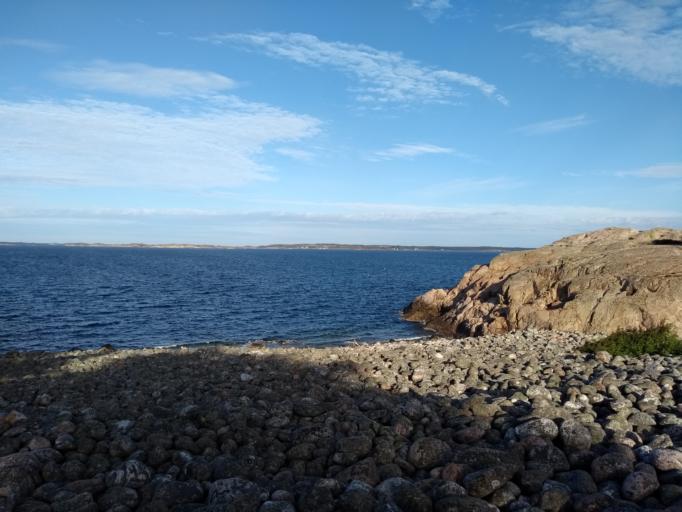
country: SE
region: Vaestra Goetaland
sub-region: Stromstads Kommun
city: Stroemstad
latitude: 58.8686
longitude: 11.1211
